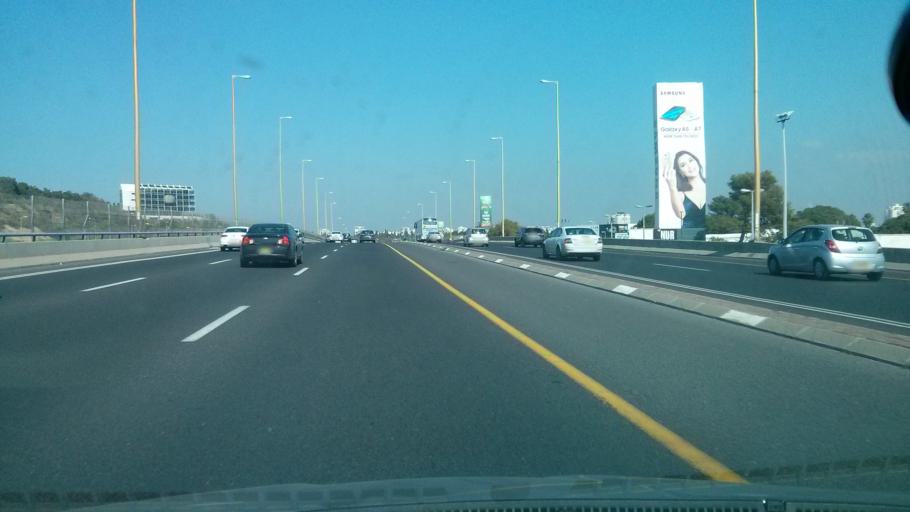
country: IL
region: Tel Aviv
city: Ramat Gan
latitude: 32.1057
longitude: 34.8063
